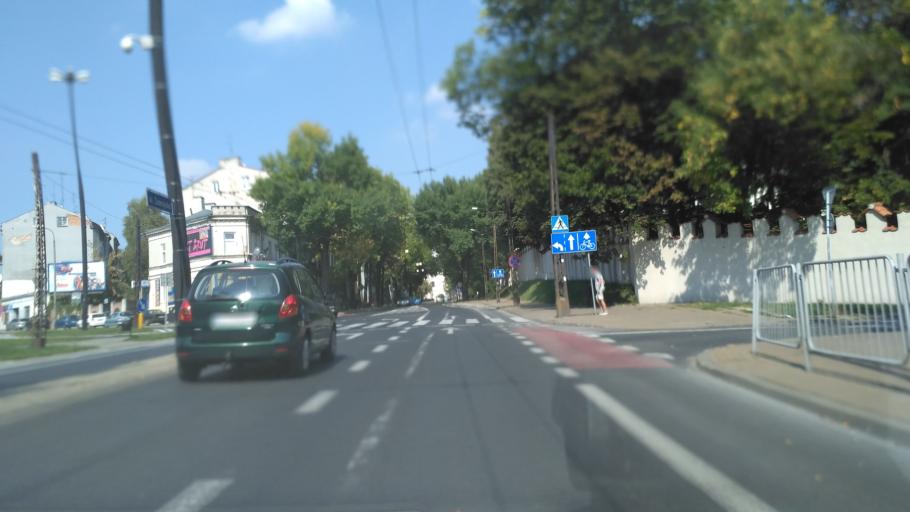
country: PL
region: Lublin Voivodeship
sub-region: Powiat lubelski
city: Lublin
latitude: 51.2428
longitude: 22.5689
